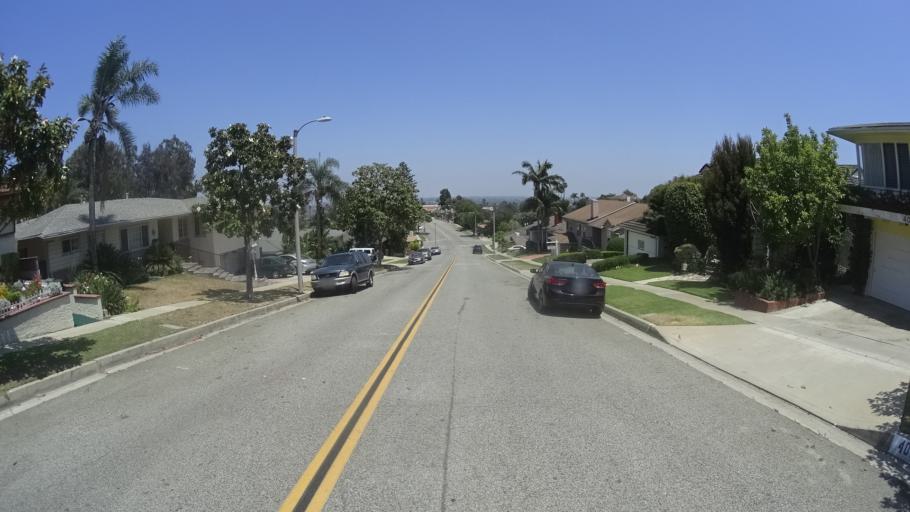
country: US
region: California
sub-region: Los Angeles County
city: View Park-Windsor Hills
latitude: 34.0018
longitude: -118.3453
